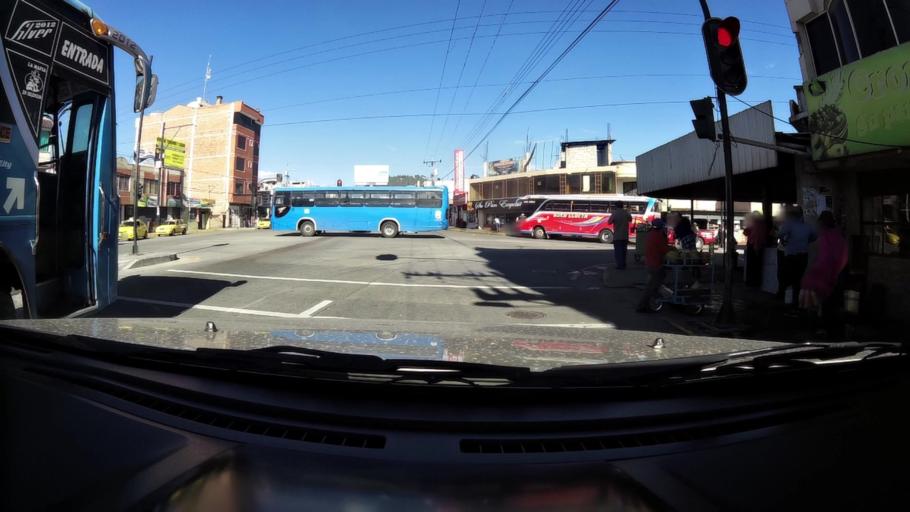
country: EC
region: Chimborazo
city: Riobamba
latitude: -1.6560
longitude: -78.6948
